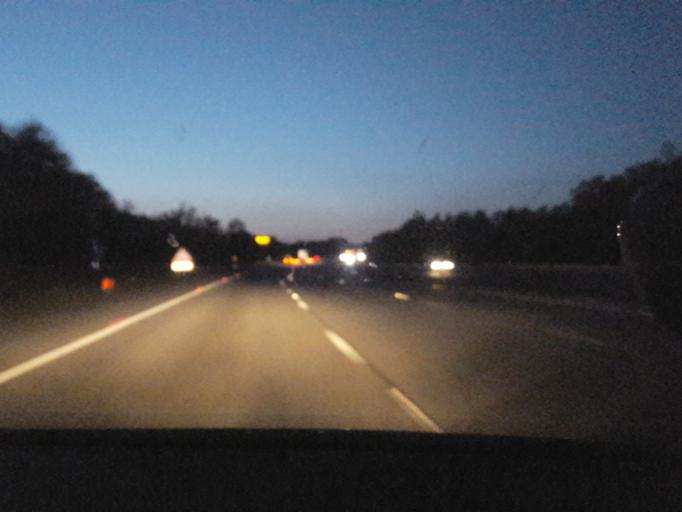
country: GB
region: England
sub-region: Leicestershire
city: Markfield
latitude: 52.6792
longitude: -1.2882
